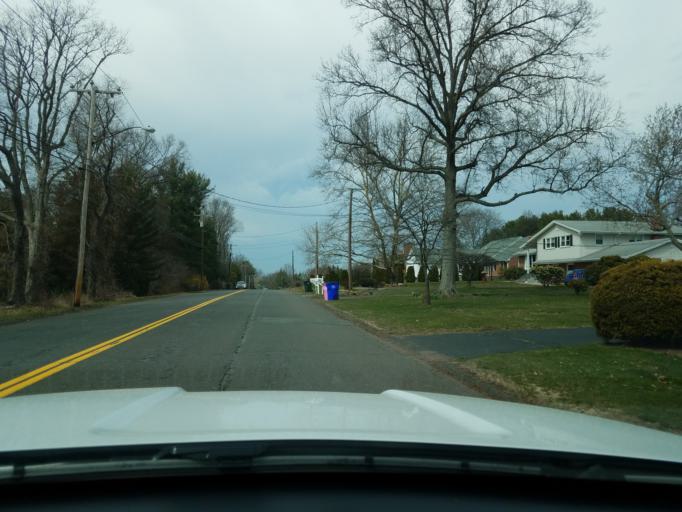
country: US
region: Connecticut
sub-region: Hartford County
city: Newington
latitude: 41.6832
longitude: -72.6911
